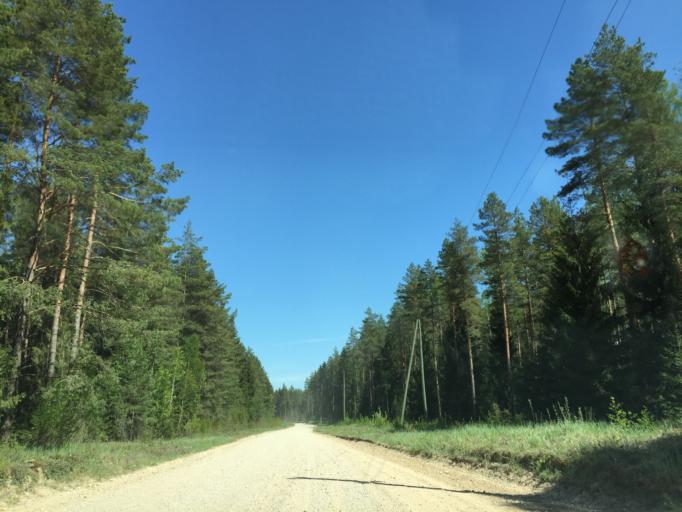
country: LV
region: Ogre
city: Ogre
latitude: 56.7464
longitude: 24.5795
